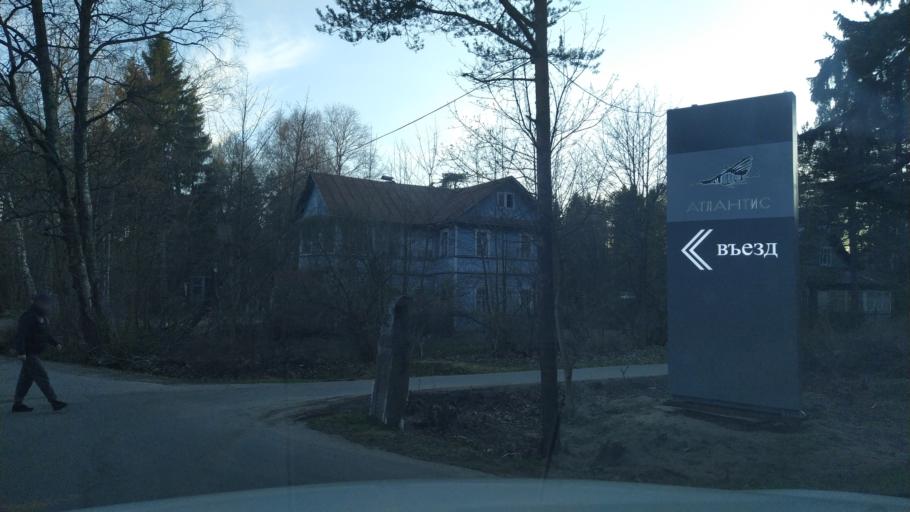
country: RU
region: St.-Petersburg
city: Solnechnoye
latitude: 60.1488
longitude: 29.9331
